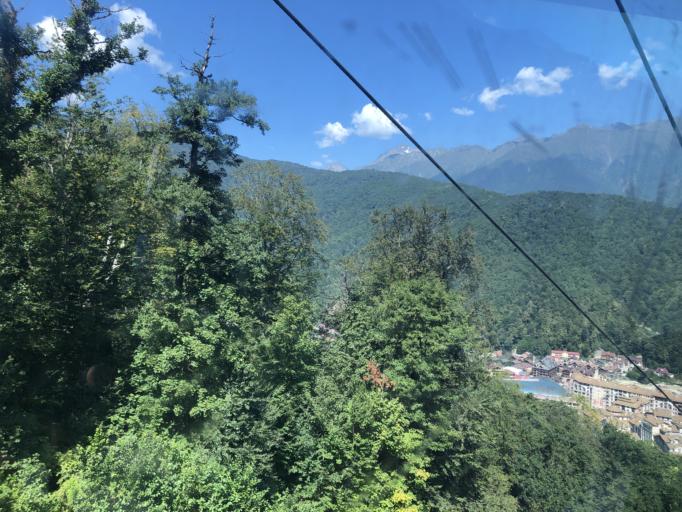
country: RU
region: Krasnodarskiy
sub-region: Sochi City
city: Krasnaya Polyana
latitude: 43.6781
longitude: 40.2641
